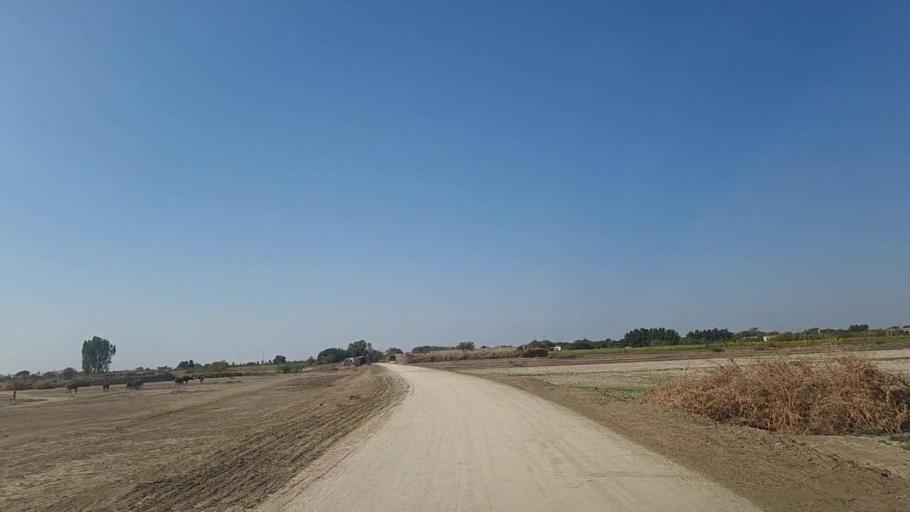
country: PK
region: Sindh
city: Naukot
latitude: 25.0091
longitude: 69.3400
